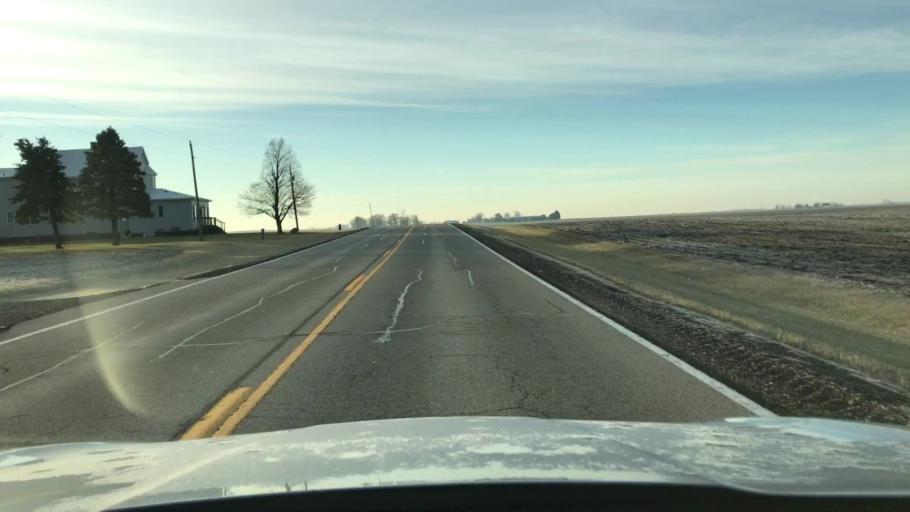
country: US
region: Illinois
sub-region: McLean County
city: Hudson
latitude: 40.6009
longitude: -88.9450
